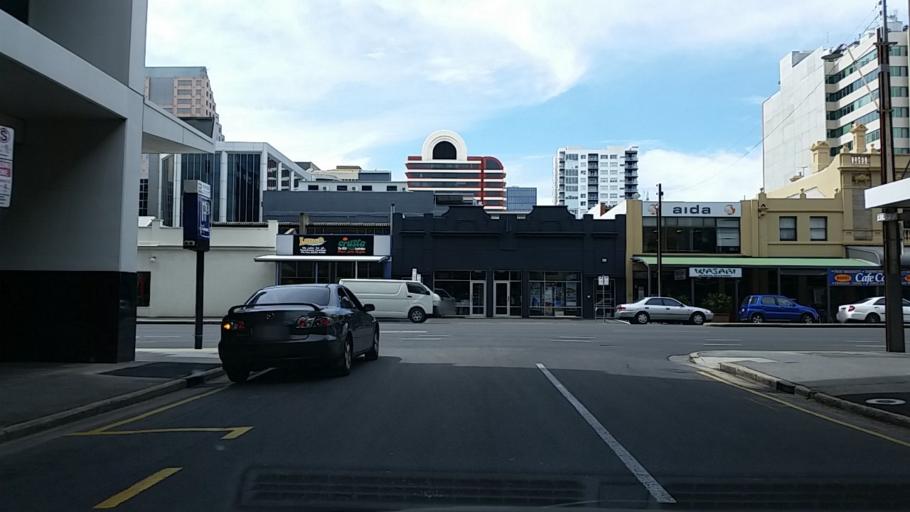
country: AU
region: South Australia
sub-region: Adelaide
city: Adelaide
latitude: -34.9272
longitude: 138.6043
